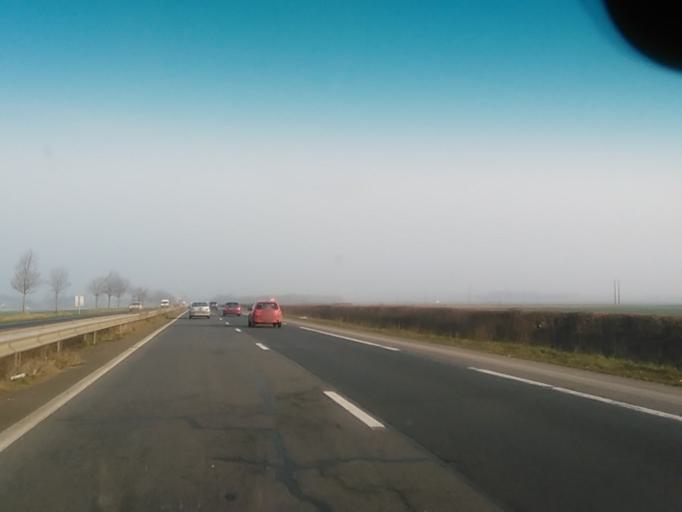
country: FR
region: Lower Normandy
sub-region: Departement du Calvados
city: Bretteville-sur-Laize
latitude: 49.0474
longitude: -0.2825
